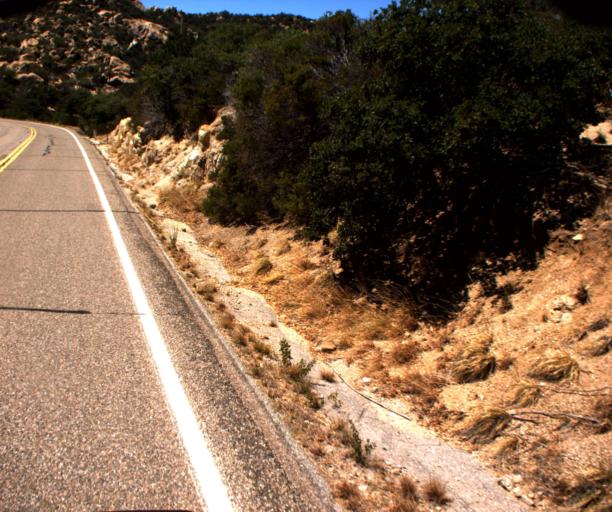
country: US
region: Arizona
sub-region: Pima County
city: Sells
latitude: 31.9508
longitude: -111.6204
